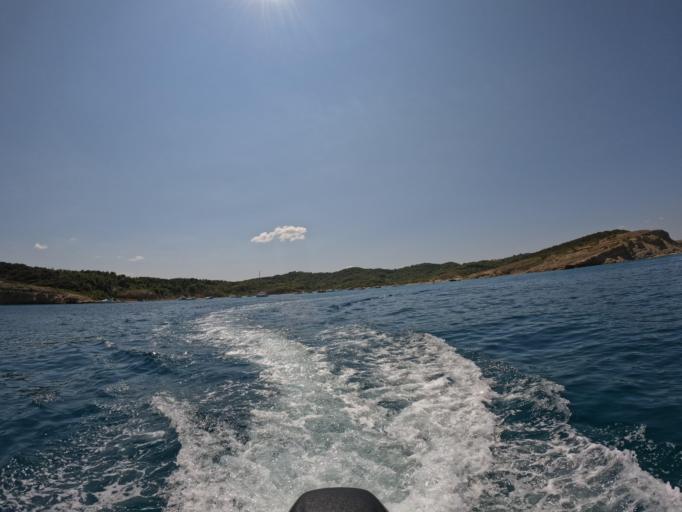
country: HR
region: Primorsko-Goranska
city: Lopar
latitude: 44.8451
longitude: 14.7566
